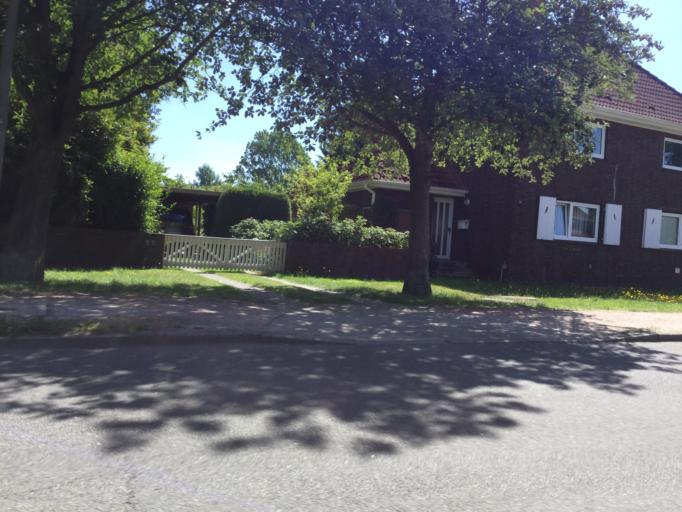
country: DE
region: Hamburg
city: Farmsen-Berne
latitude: 53.6306
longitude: 10.1329
